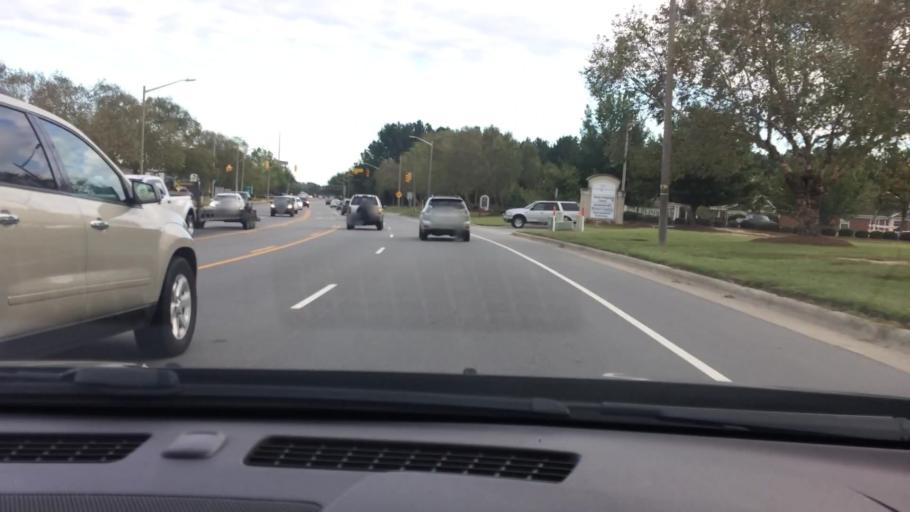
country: US
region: North Carolina
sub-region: Pitt County
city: Summerfield
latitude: 35.6022
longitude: -77.4115
